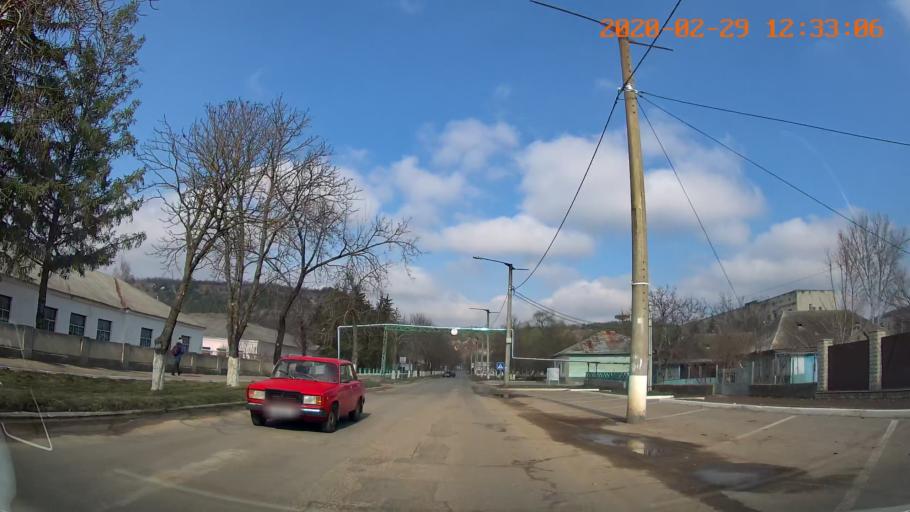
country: MD
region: Telenesti
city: Camenca
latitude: 48.0330
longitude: 28.7033
